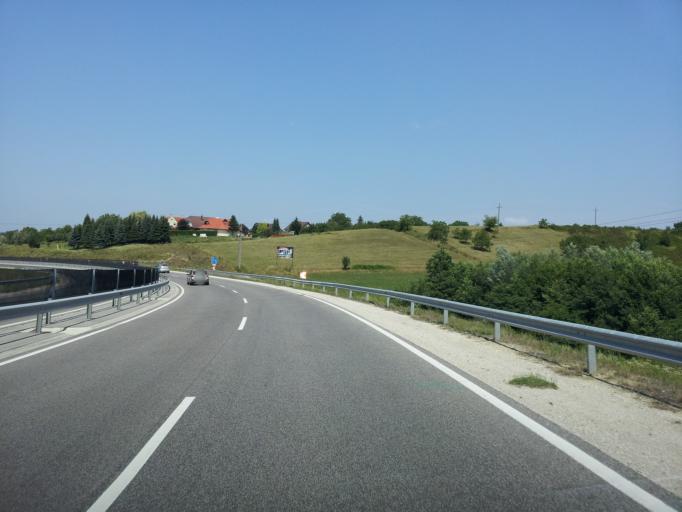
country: HU
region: Zala
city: Zalaegerszeg
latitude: 46.8399
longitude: 16.8851
